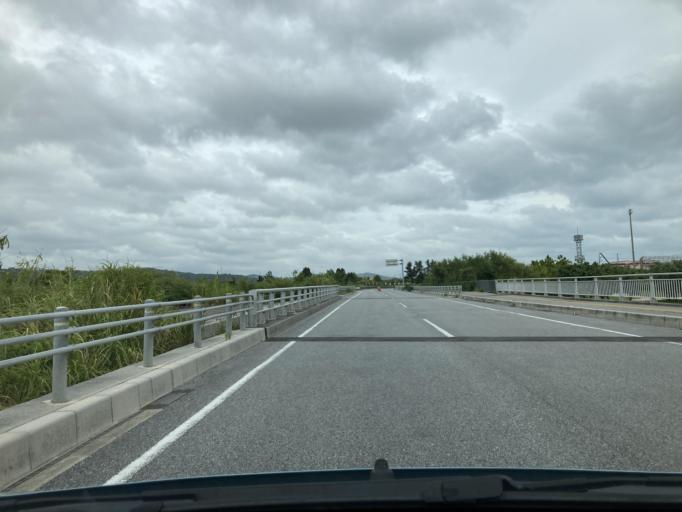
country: JP
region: Okinawa
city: Ginowan
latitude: 26.2160
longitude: 127.7722
